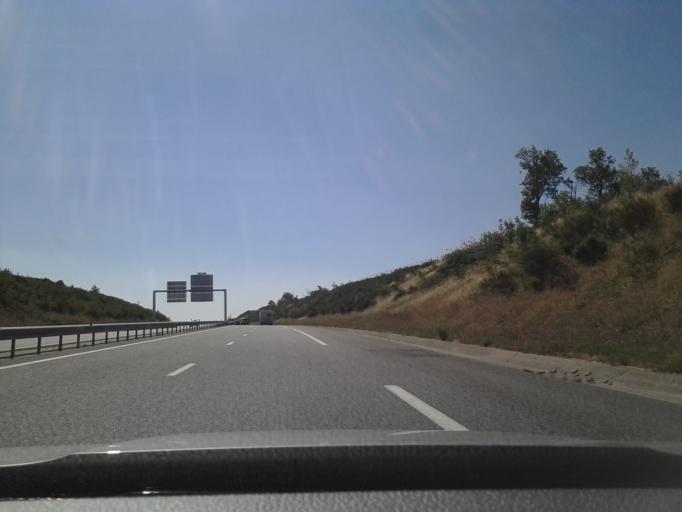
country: FR
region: Midi-Pyrenees
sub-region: Departement de l'Aveyron
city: La Cavalerie
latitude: 44.0019
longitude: 3.1538
